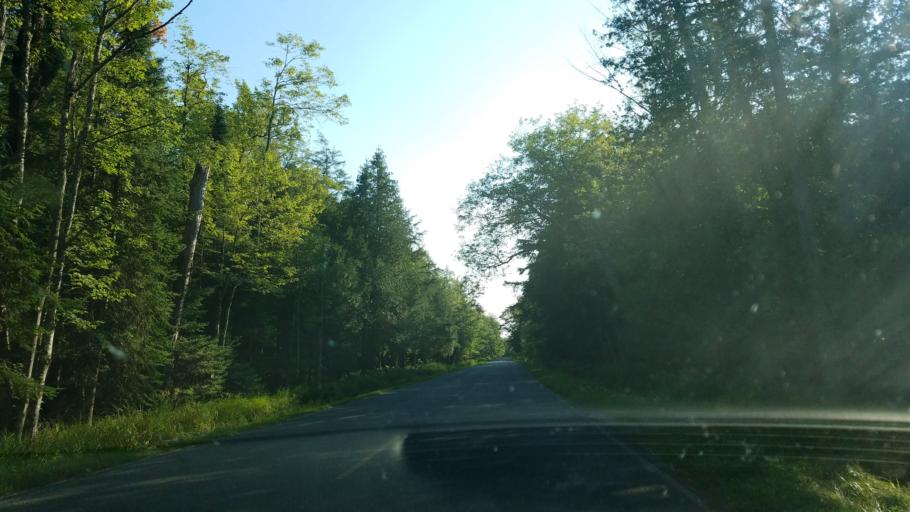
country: US
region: Wisconsin
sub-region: Bayfield County
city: Washburn
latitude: 46.7665
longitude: -90.7507
